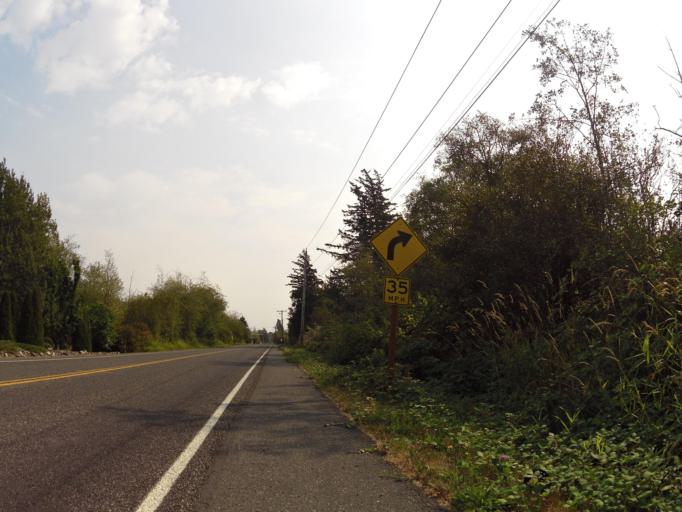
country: US
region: Washington
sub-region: Whatcom County
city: Marietta-Alderwood
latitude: 48.7897
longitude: -122.5651
